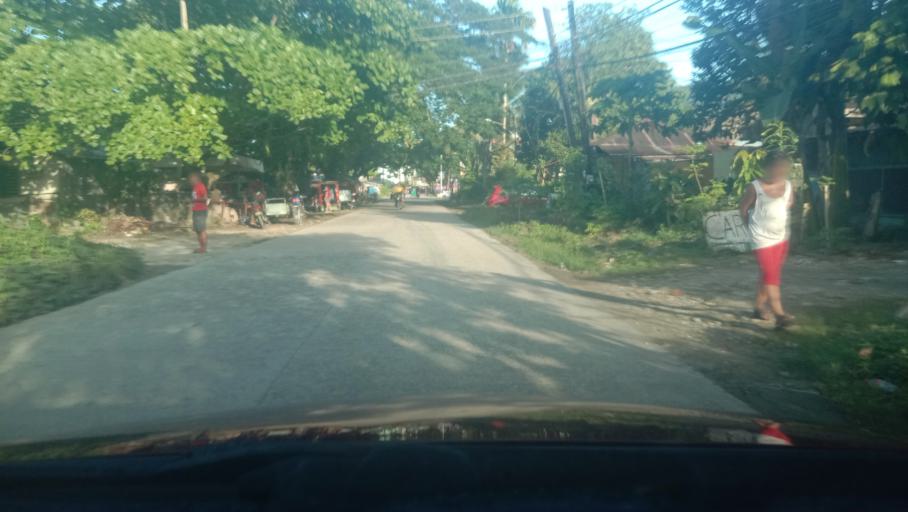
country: PH
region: Caraga
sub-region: Province of Agusan del Sur
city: San Francisco
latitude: 8.5101
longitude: 125.9747
